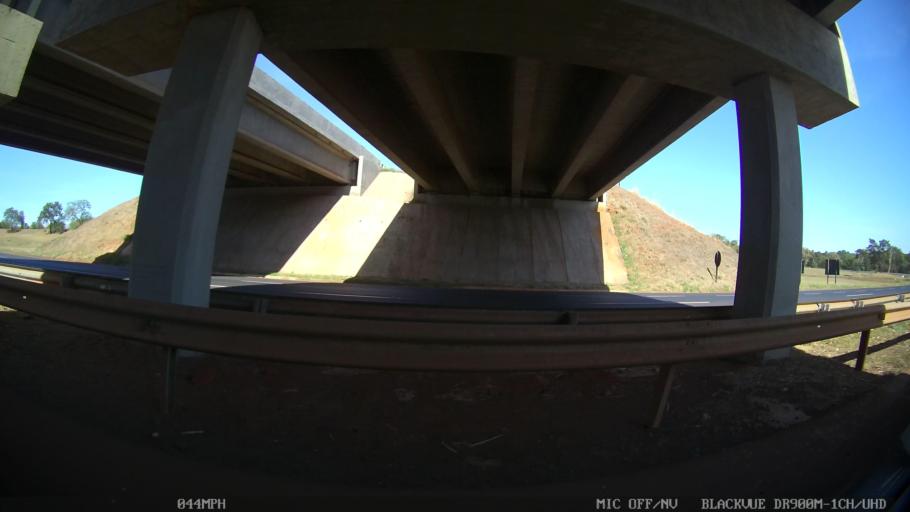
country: BR
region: Sao Paulo
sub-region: Barretos
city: Barretos
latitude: -20.5321
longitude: -48.5989
